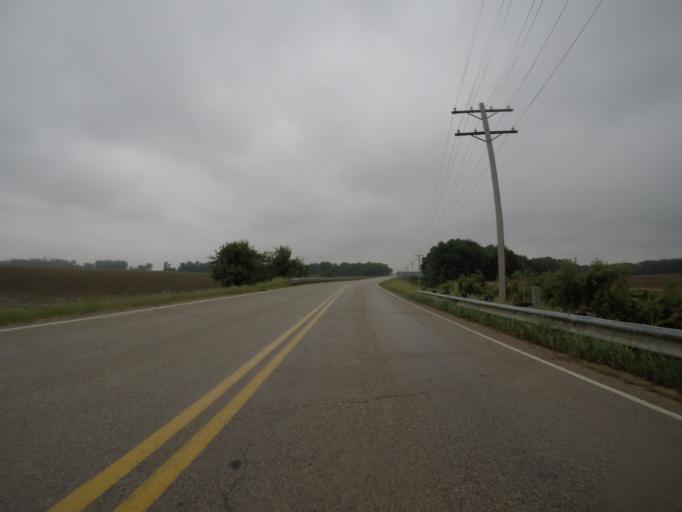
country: US
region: Kansas
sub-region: Pottawatomie County
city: Wamego
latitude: 39.2360
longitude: -96.2313
